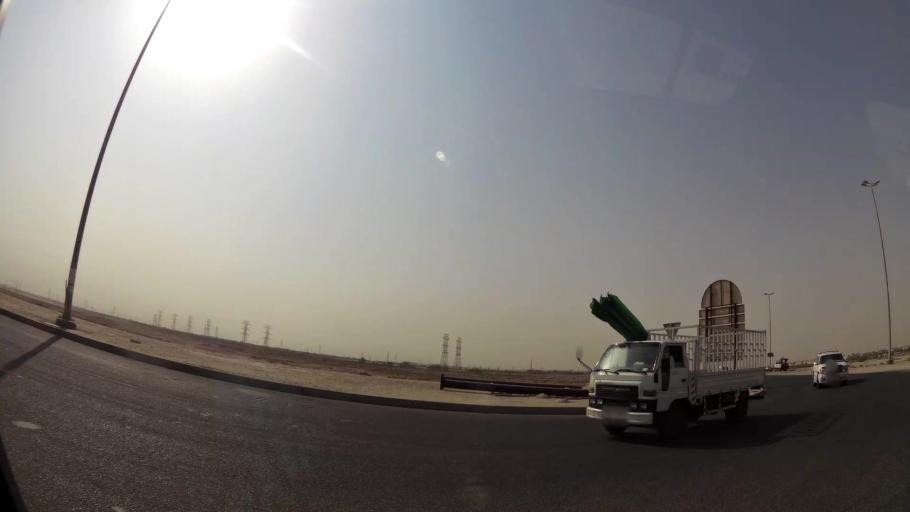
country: KW
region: Muhafazat al Jahra'
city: Al Jahra'
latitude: 29.3328
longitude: 47.7573
